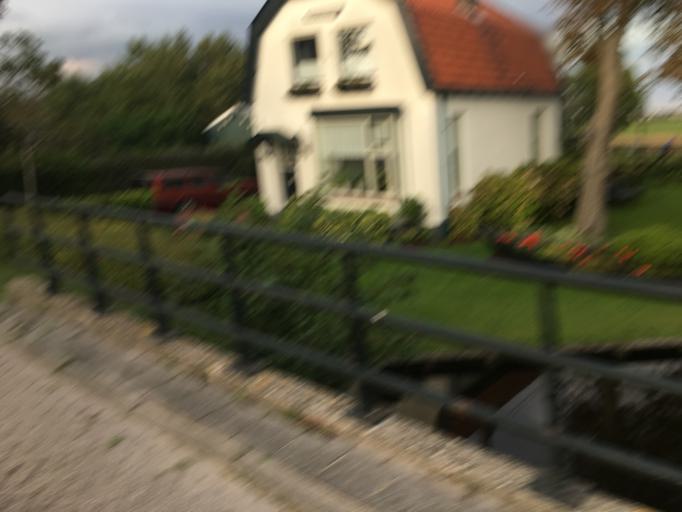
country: NL
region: North Holland
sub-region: Gemeente Zaanstad
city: Zaanstad
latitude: 52.4483
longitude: 4.7764
